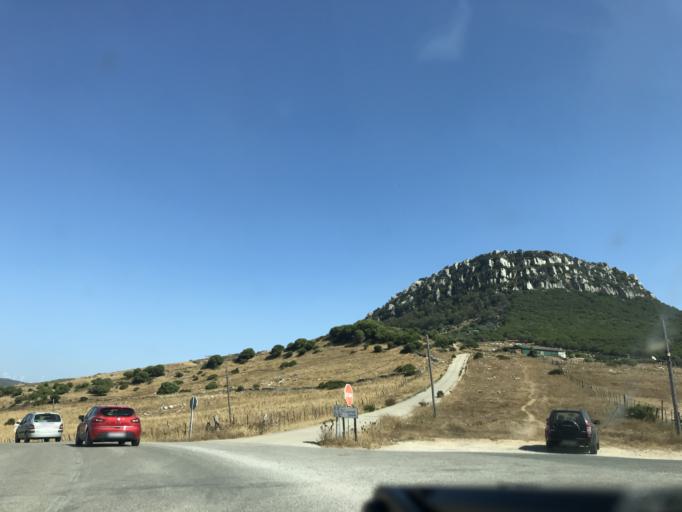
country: ES
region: Andalusia
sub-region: Provincia de Cadiz
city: Zahara de los Atunes
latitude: 36.1006
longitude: -5.7328
